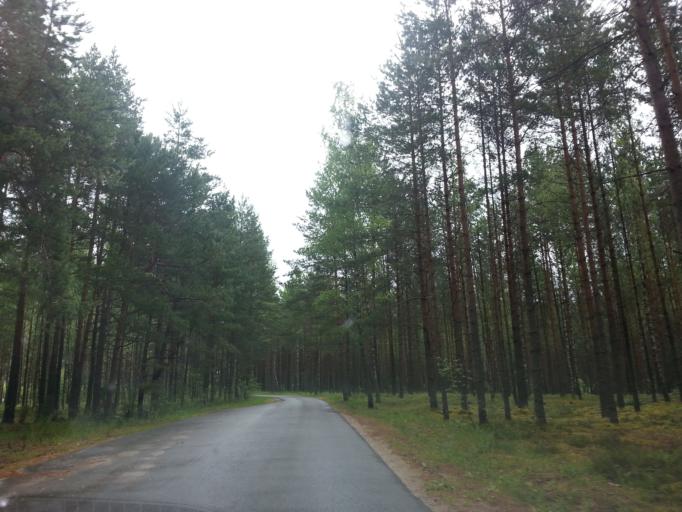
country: BY
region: Minsk
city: Narach
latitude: 54.8614
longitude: 26.6928
